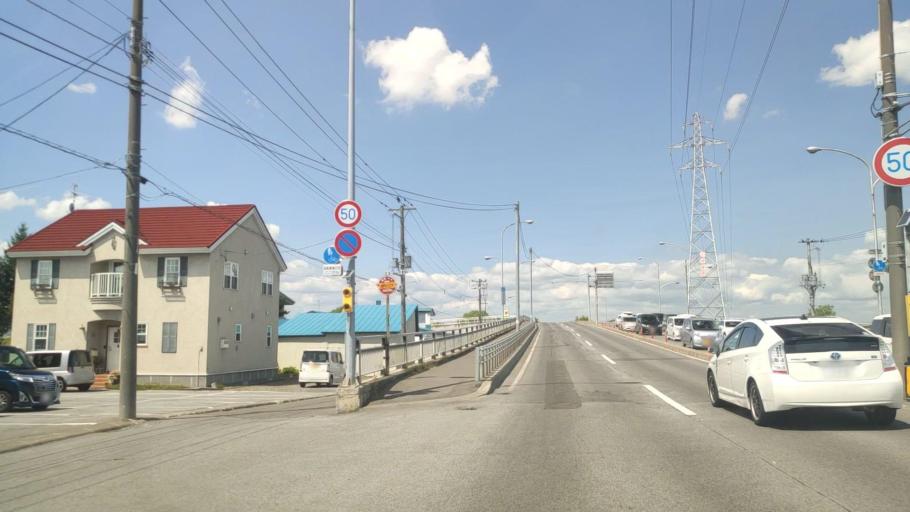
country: JP
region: Hokkaido
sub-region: Asahikawa-shi
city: Asahikawa
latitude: 43.7957
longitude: 142.3986
